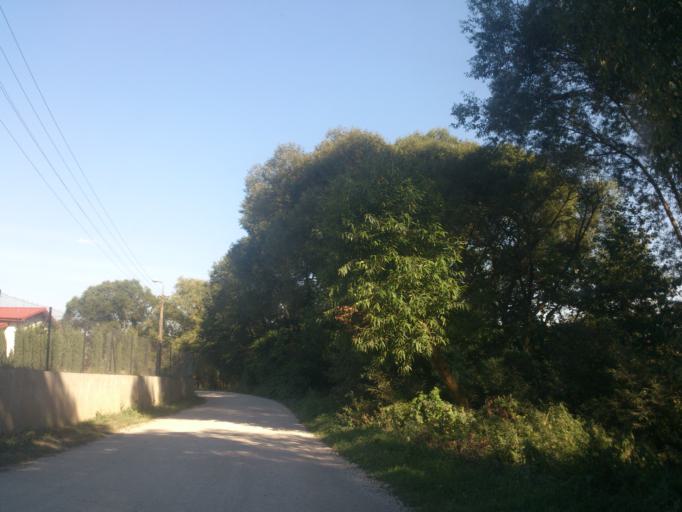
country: PL
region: Kujawsko-Pomorskie
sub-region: Powiat golubsko-dobrzynski
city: Ciechocin
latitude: 53.0610
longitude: 18.9270
